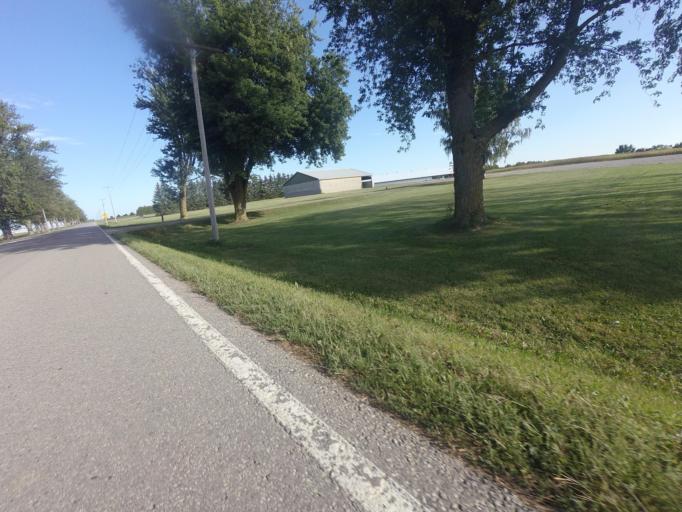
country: CA
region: Ontario
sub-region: Wellington County
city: Guelph
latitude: 43.6393
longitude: -80.4002
